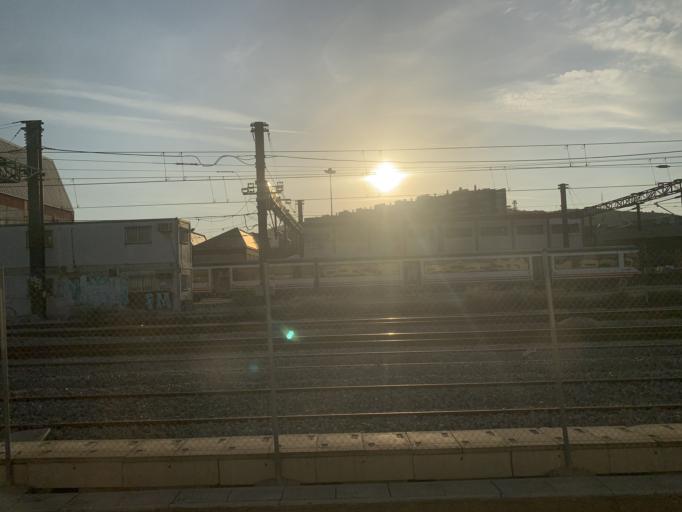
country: ES
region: Catalonia
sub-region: Provincia de Barcelona
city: Sant Andreu de Palomar
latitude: 41.4460
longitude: 2.1966
